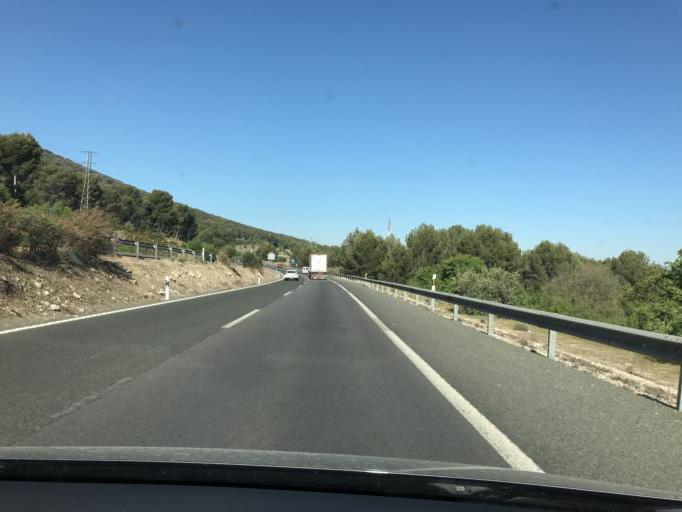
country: ES
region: Andalusia
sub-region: Provincia de Granada
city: Loja
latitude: 37.1601
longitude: -4.1491
